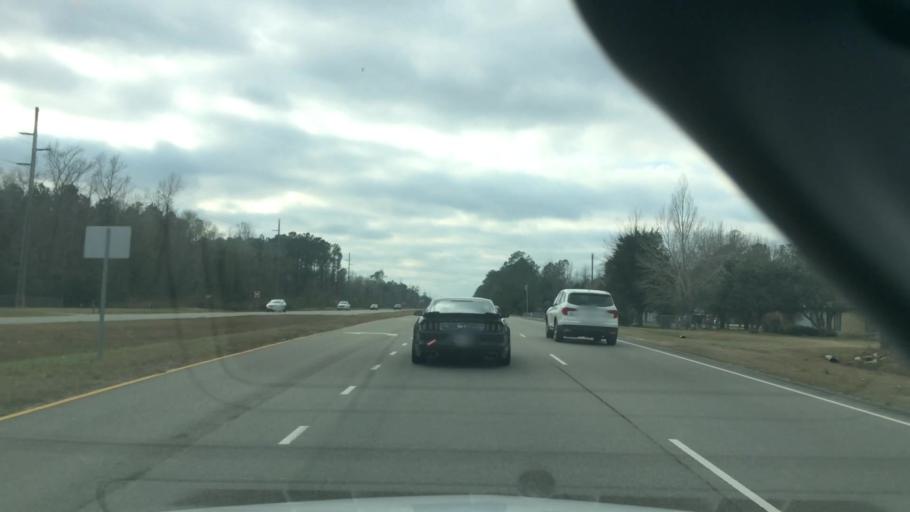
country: US
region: North Carolina
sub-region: Brunswick County
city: Shallotte
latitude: 34.0063
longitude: -78.3044
